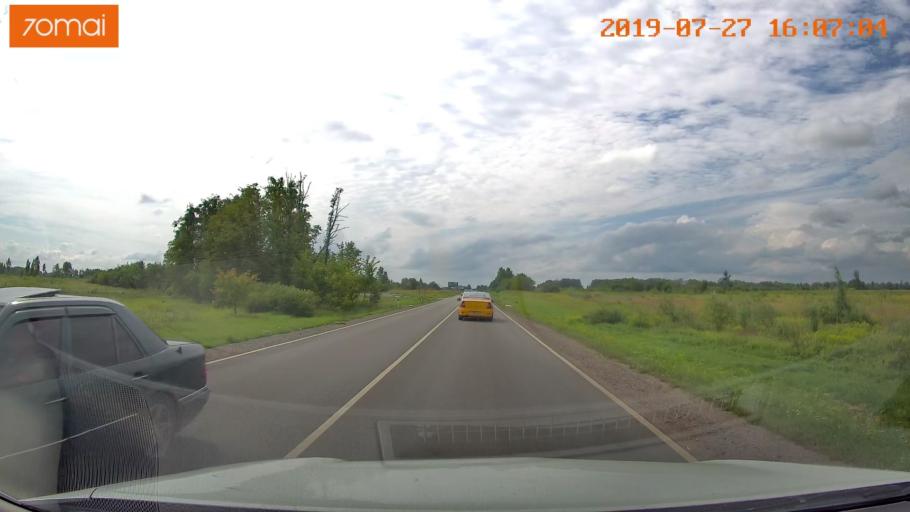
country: RU
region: Kaliningrad
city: Chernyakhovsk
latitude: 54.6348
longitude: 21.7655
